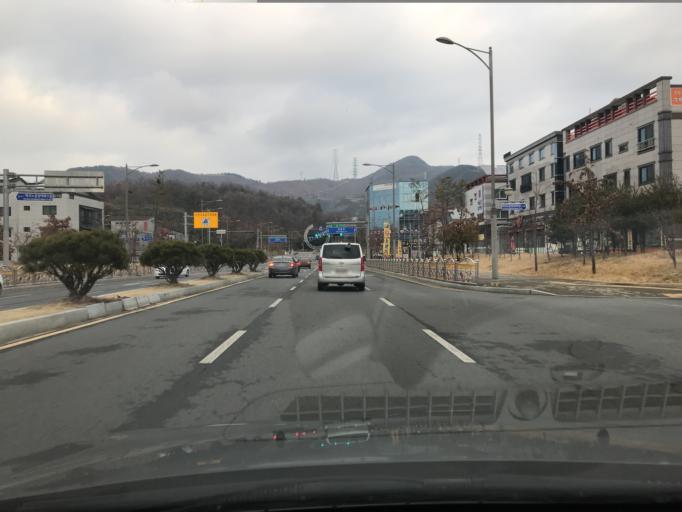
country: KR
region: Daegu
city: Hwawon
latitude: 35.6975
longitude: 128.4578
